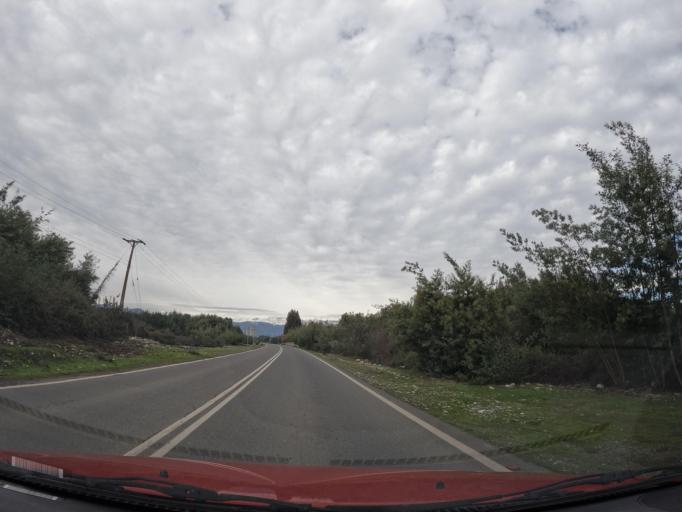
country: CL
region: Maule
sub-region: Provincia de Linares
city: Linares
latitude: -35.9069
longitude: -71.4990
